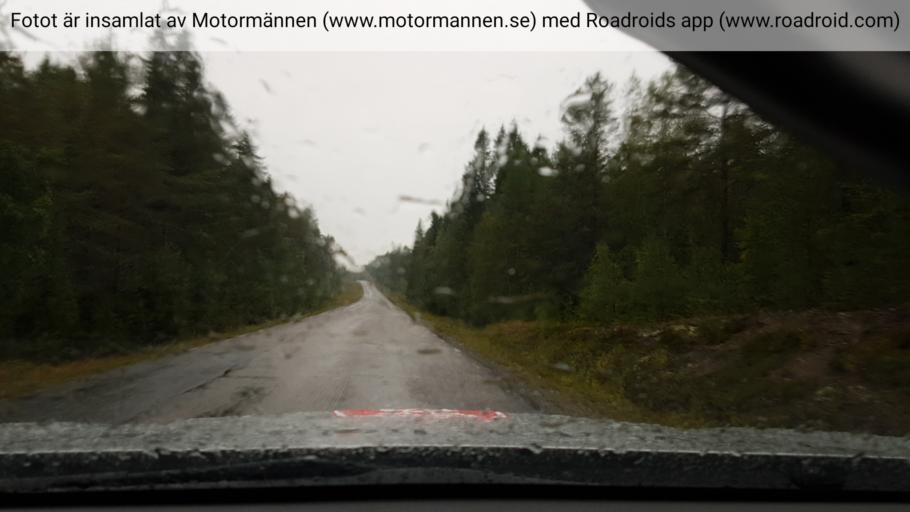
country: SE
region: Vaesterbotten
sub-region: Skelleftea Kommun
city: Burea
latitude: 64.3743
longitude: 21.2866
